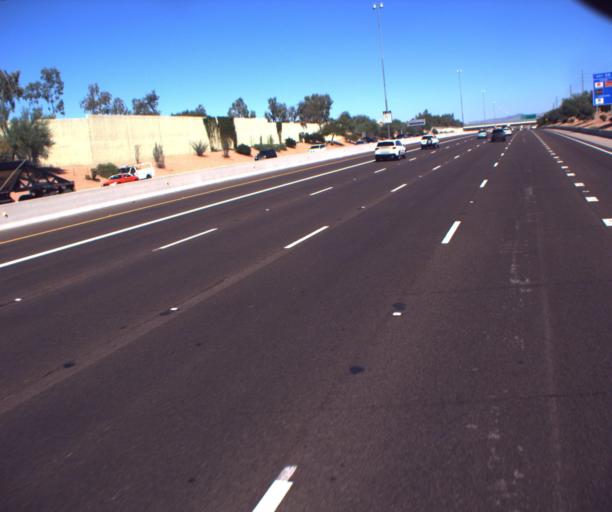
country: US
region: Arizona
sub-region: Maricopa County
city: Paradise Valley
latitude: 33.6059
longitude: -111.8913
